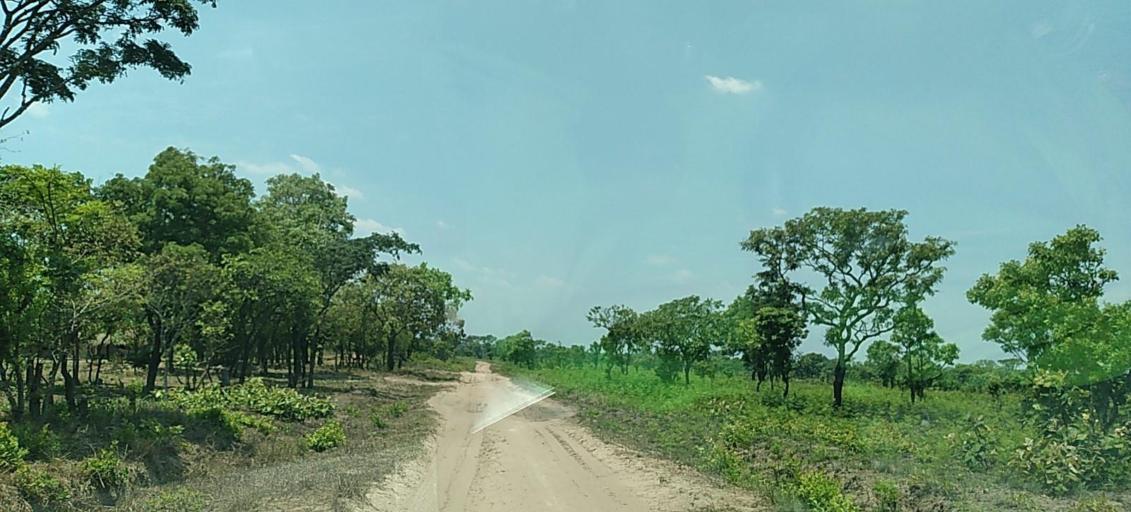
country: CD
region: Katanga
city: Kolwezi
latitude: -11.3359
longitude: 25.2243
